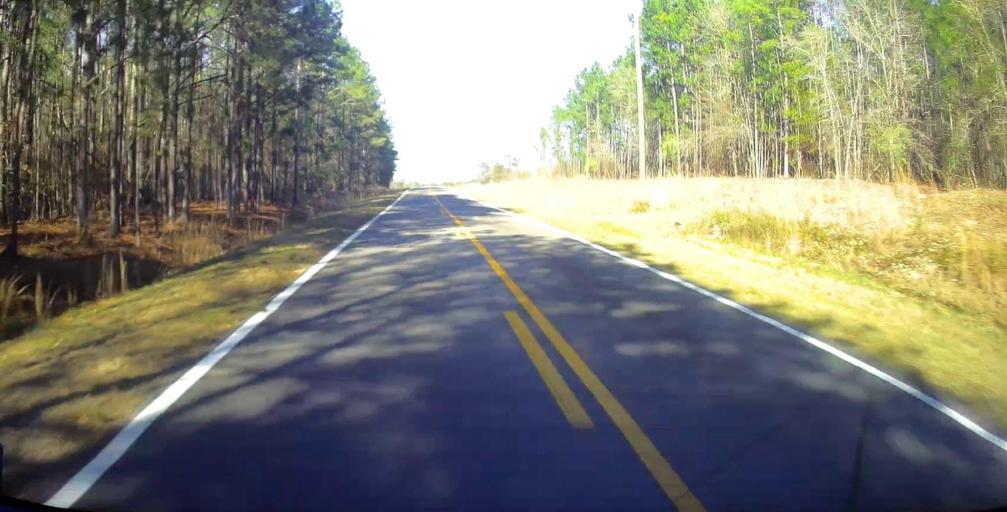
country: US
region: Georgia
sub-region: Taylor County
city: Reynolds
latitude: 32.5778
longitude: -83.9943
